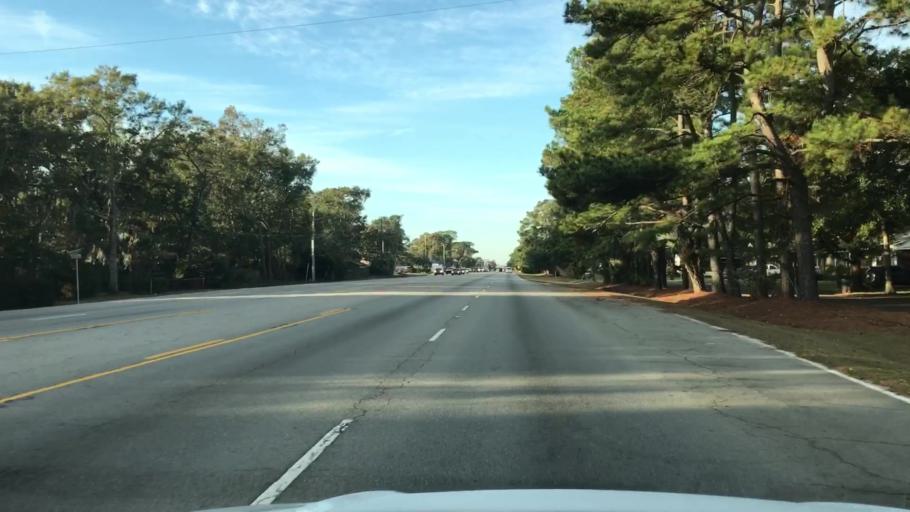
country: US
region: South Carolina
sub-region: Charleston County
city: North Charleston
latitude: 32.8119
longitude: -80.0017
